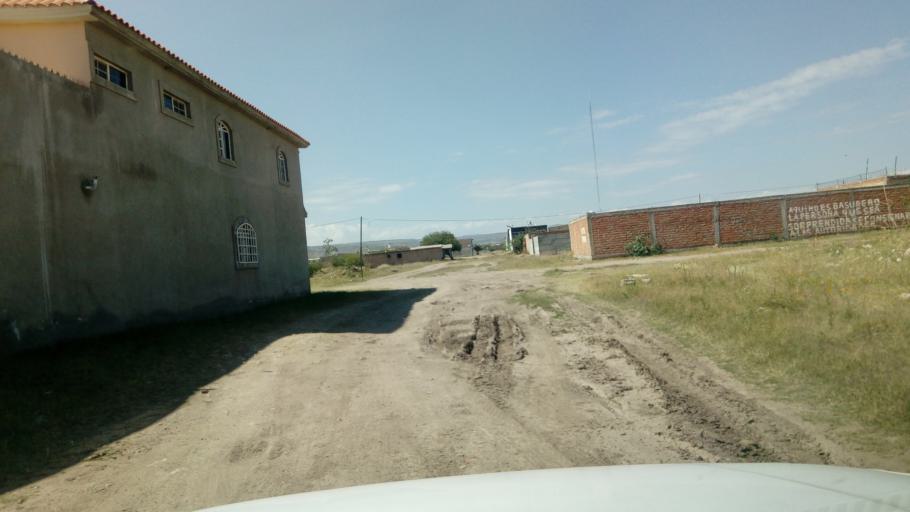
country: MX
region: Durango
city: Victoria de Durango
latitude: 23.9876
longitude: -104.6819
